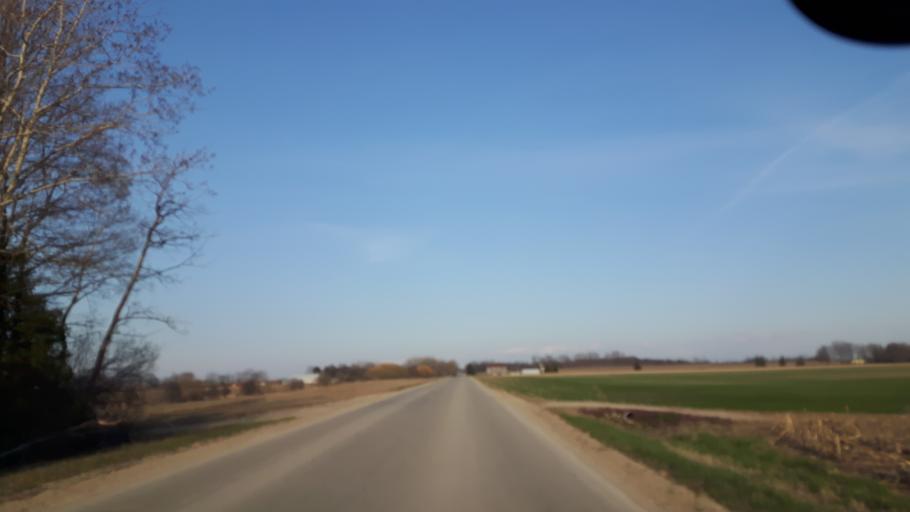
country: CA
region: Ontario
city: Goderich
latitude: 43.6983
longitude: -81.6958
